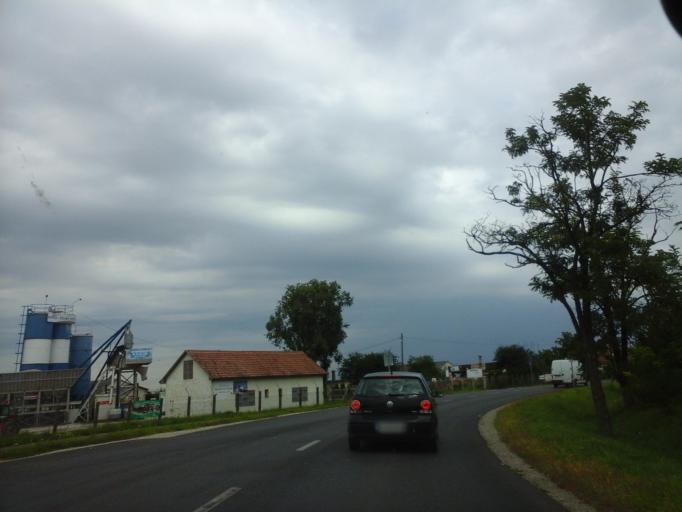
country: HU
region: Hajdu-Bihar
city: Balmazujvaros
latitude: 47.6006
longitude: 21.3354
